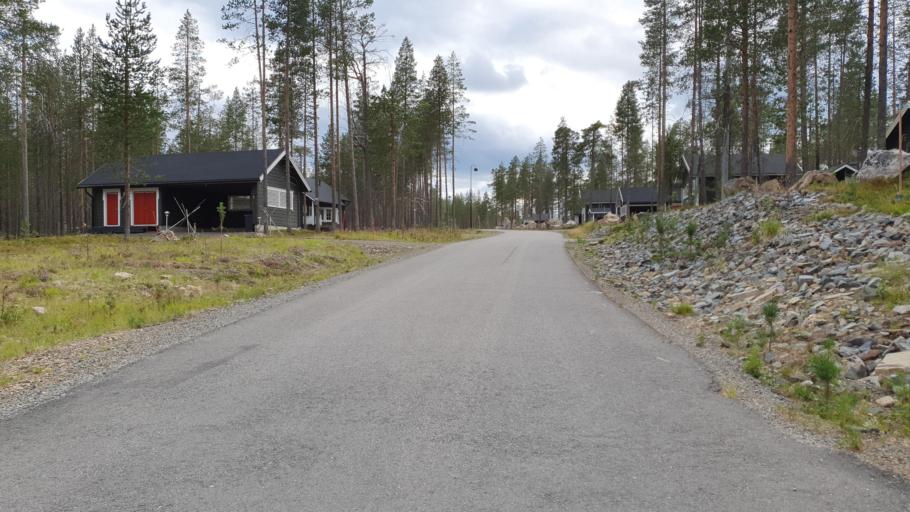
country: FI
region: Lapland
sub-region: Tunturi-Lappi
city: Kolari
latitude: 67.5903
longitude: 24.1239
